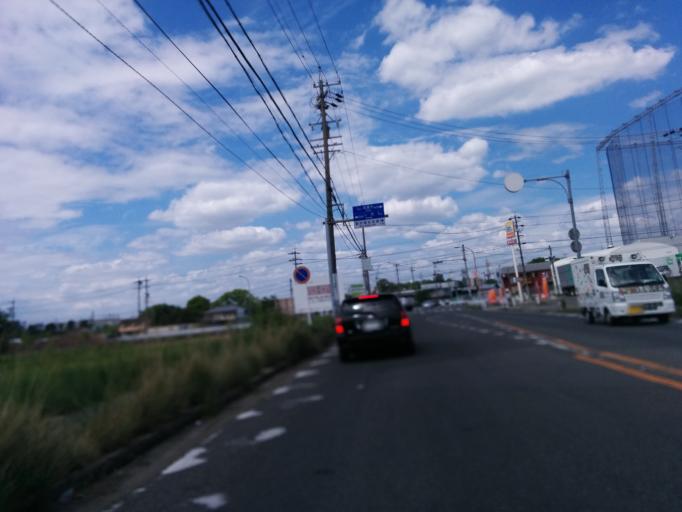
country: JP
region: Aichi
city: Kasugai
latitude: 35.2737
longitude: 136.9861
